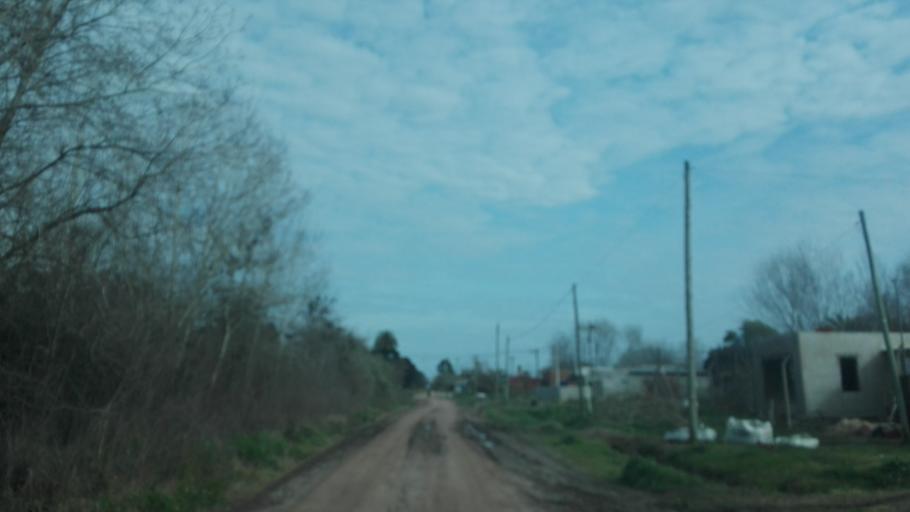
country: AR
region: Buenos Aires
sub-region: Partido de Chascomus
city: Chascomus
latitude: -35.5817
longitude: -57.9853
